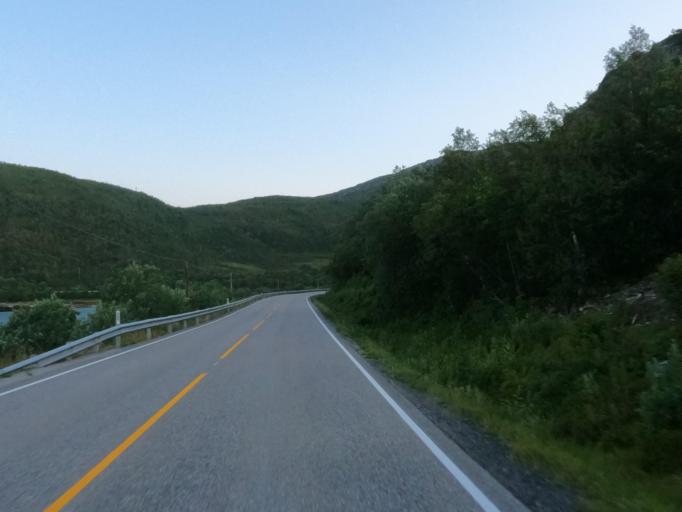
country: NO
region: Nordland
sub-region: Lodingen
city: Lodingen
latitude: 68.4945
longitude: 16.0909
